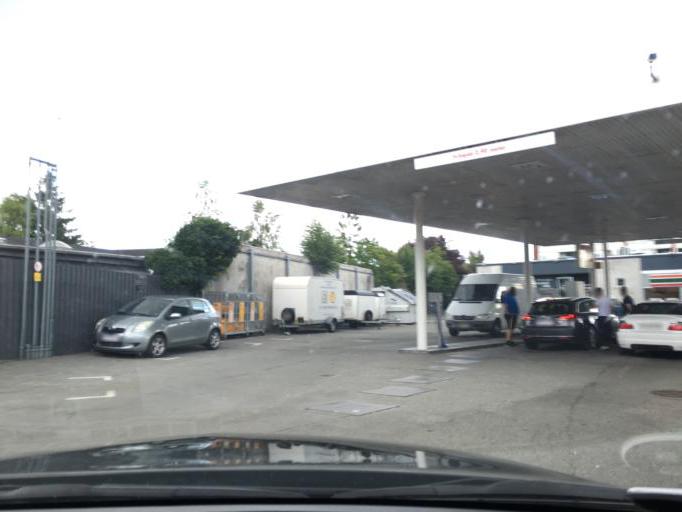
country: DK
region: Capital Region
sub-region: Herlev Kommune
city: Herlev
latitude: 55.7136
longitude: 12.4670
